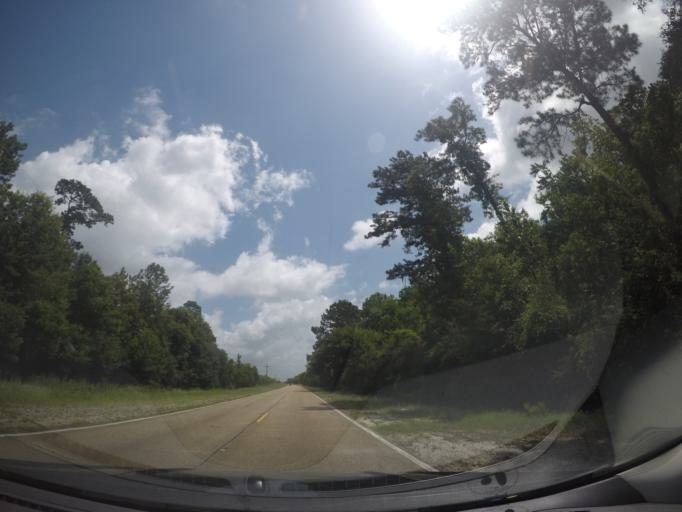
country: US
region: Mississippi
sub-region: Hancock County
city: Pearlington
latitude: 30.2072
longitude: -89.6973
